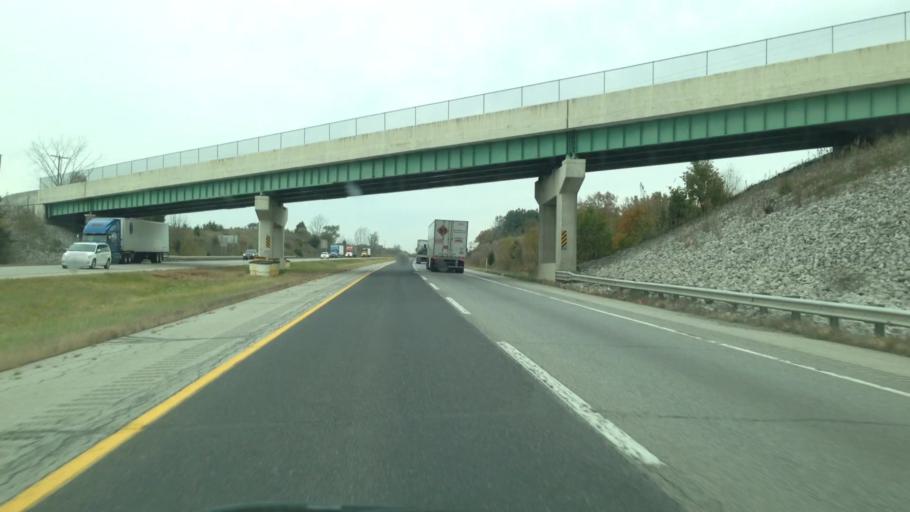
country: US
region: Indiana
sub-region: Steuben County
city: Fremont
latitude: 41.6728
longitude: -84.8663
